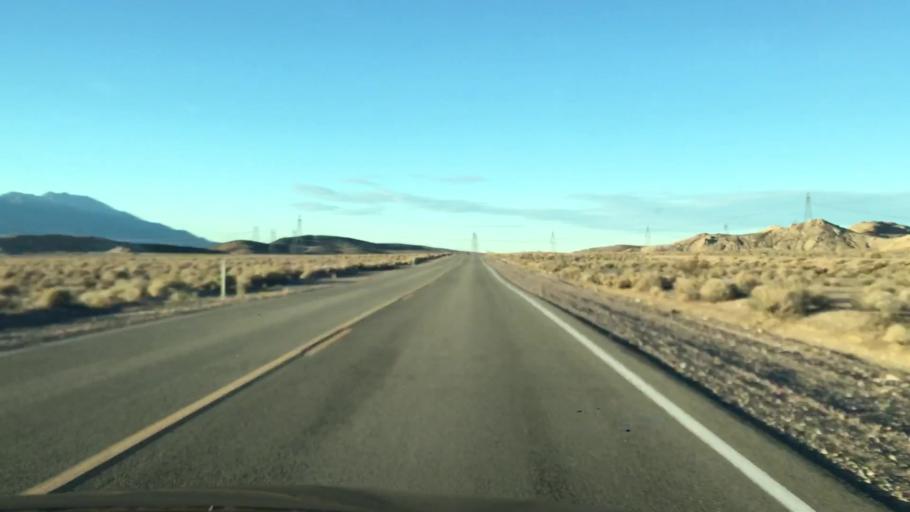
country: US
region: California
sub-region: San Bernardino County
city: Fort Irwin
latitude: 35.3771
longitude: -116.1218
